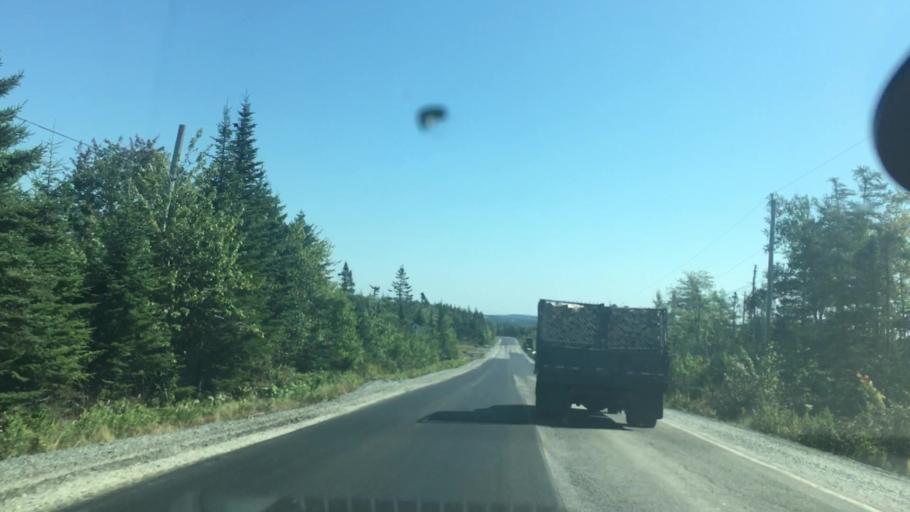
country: CA
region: Nova Scotia
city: New Glasgow
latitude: 44.8982
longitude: -62.4287
